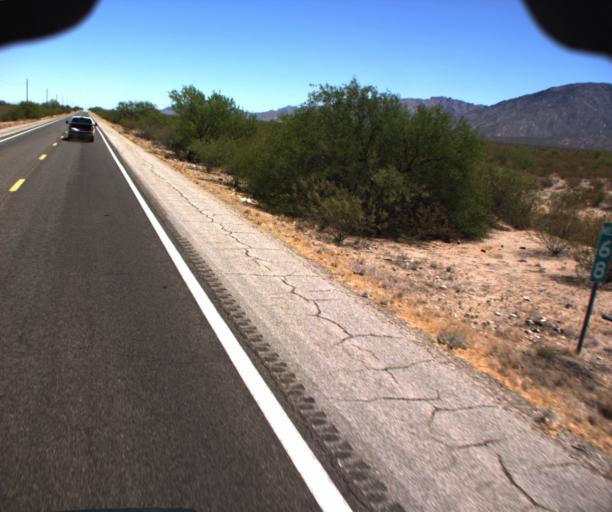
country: US
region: Arizona
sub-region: La Paz County
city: Salome
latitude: 33.8549
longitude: -113.4375
